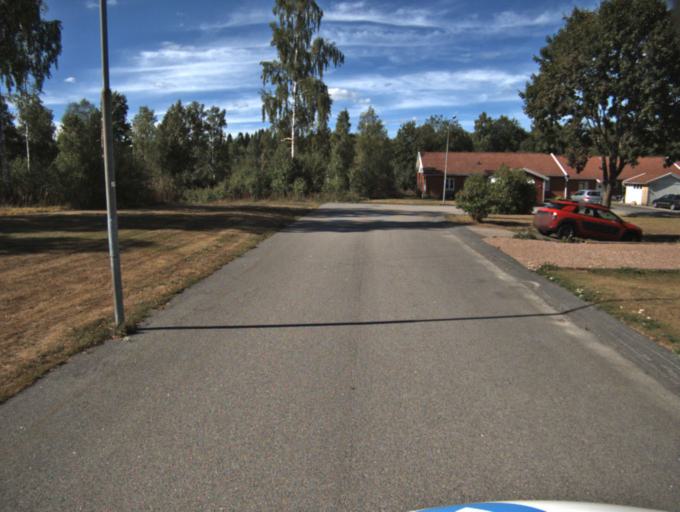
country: SE
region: Vaestra Goetaland
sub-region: Ulricehamns Kommun
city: Ulricehamn
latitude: 57.6952
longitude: 13.5785
